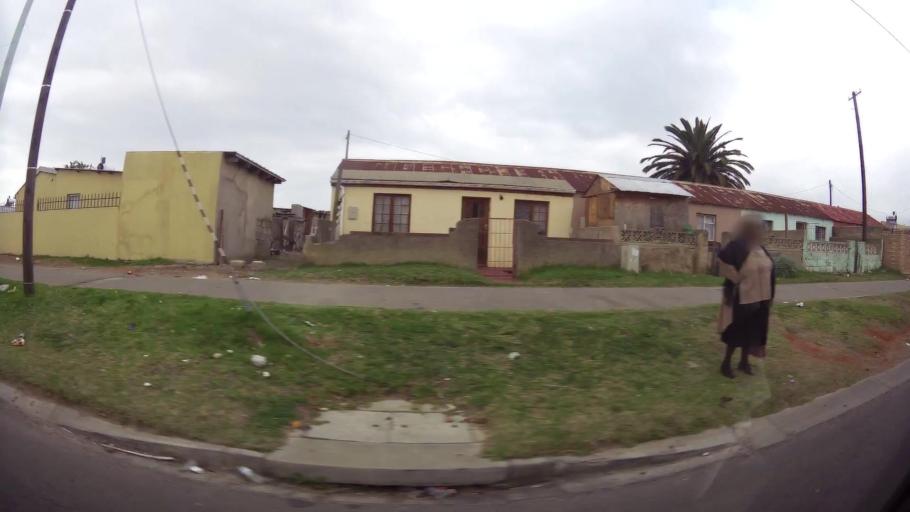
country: ZA
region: Eastern Cape
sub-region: Nelson Mandela Bay Metropolitan Municipality
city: Port Elizabeth
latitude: -33.9013
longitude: 25.5993
